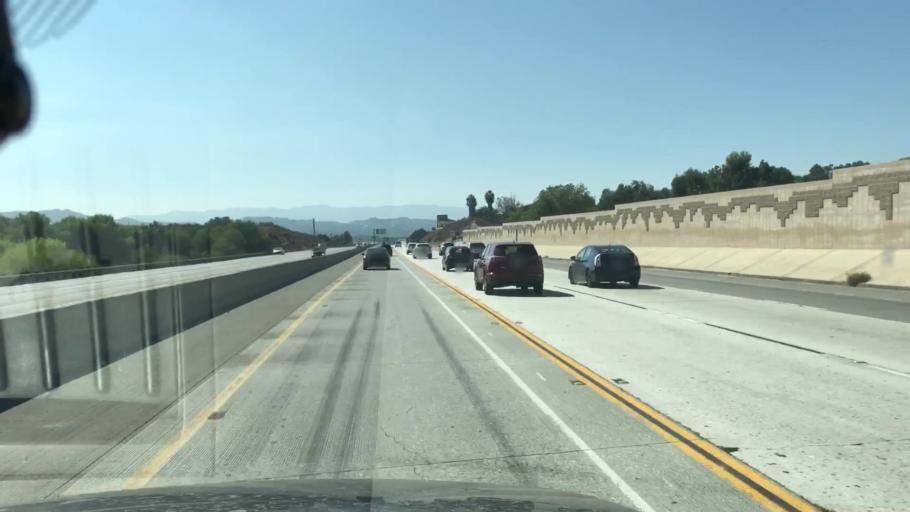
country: US
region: California
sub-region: Los Angeles County
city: Santa Clarita
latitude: 34.4233
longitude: -118.4281
